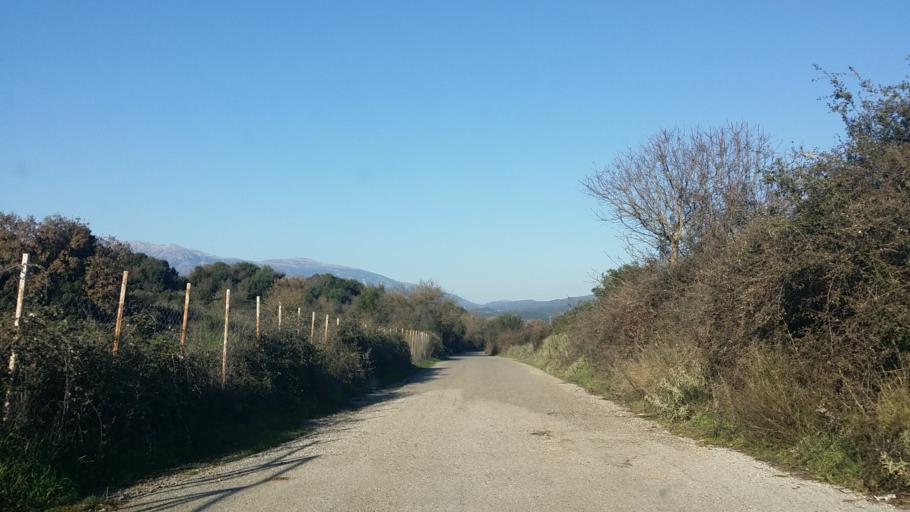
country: GR
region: West Greece
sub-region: Nomos Aitolias kai Akarnanias
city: Katouna
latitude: 38.7615
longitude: 21.1412
